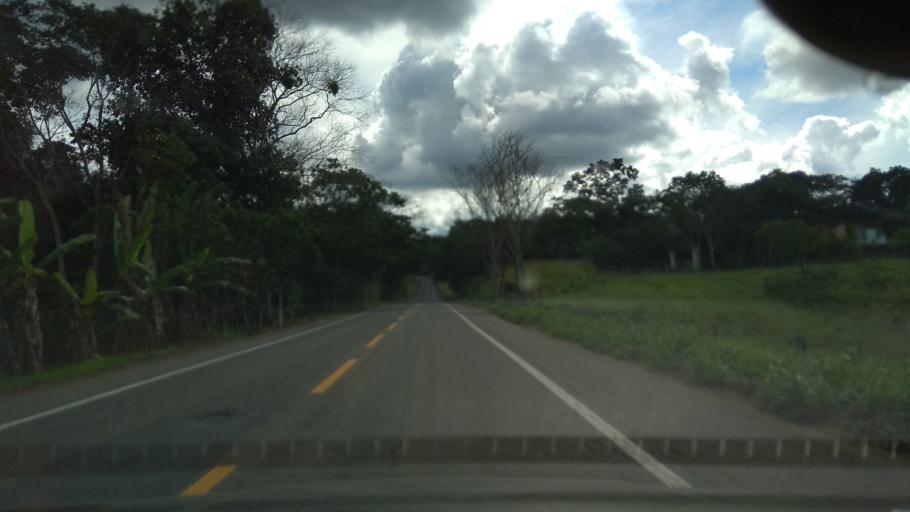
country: BR
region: Bahia
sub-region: Ubaitaba
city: Ubaitaba
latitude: -14.2650
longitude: -39.3295
